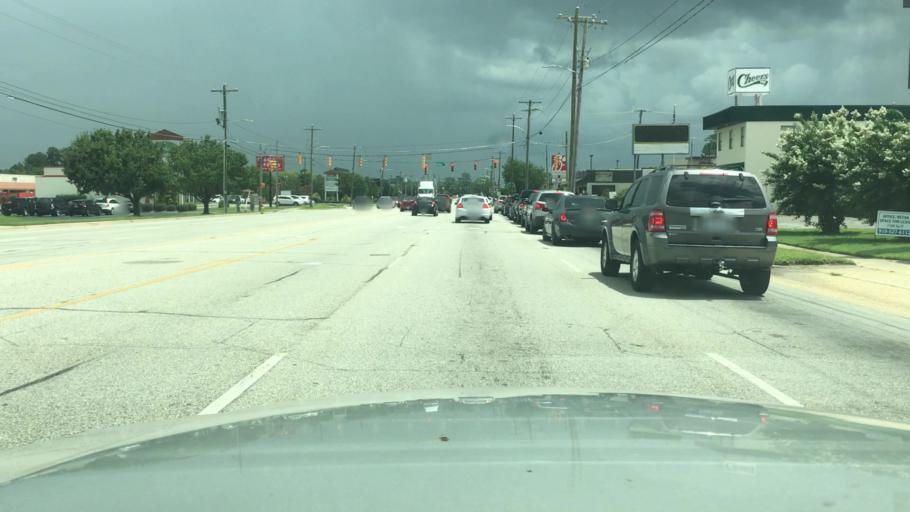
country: US
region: North Carolina
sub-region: Cumberland County
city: Fayetteville
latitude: 35.0450
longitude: -78.9256
